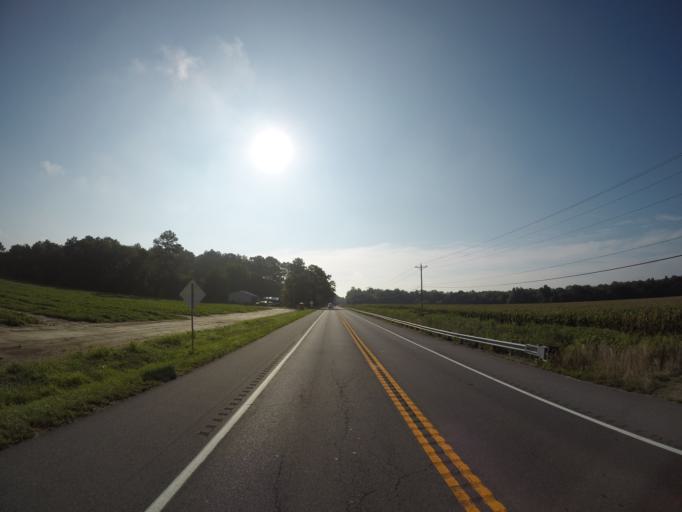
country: US
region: Delaware
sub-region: Sussex County
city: Bridgeville
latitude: 38.7099
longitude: -75.5280
